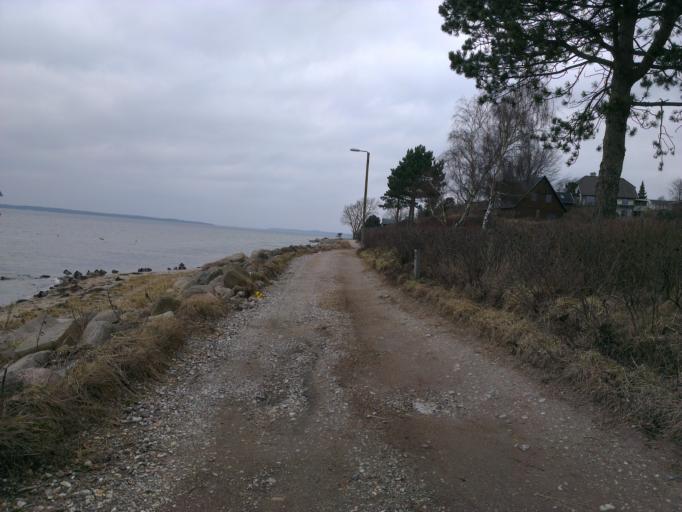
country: DK
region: Capital Region
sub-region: Frederikssund Kommune
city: Frederikssund
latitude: 55.8492
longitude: 12.0442
